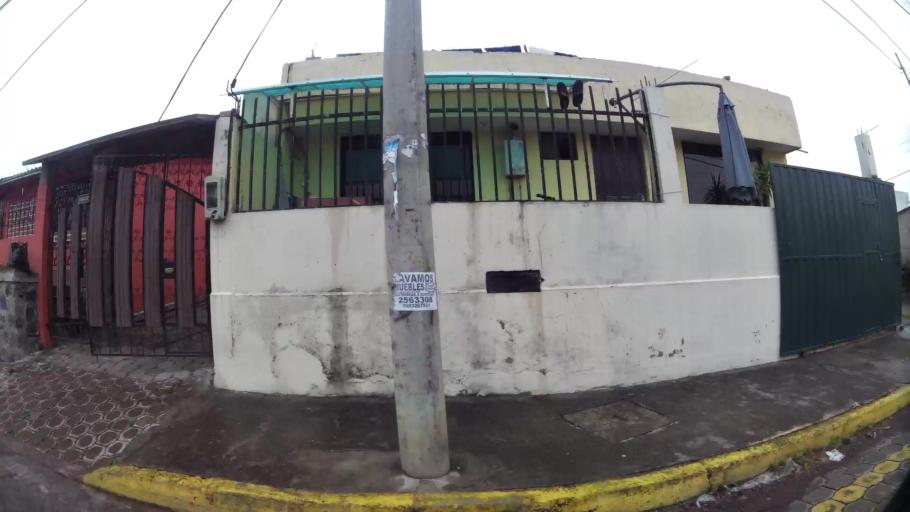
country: EC
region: Pichincha
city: Sangolqui
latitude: -0.2953
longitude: -78.4405
